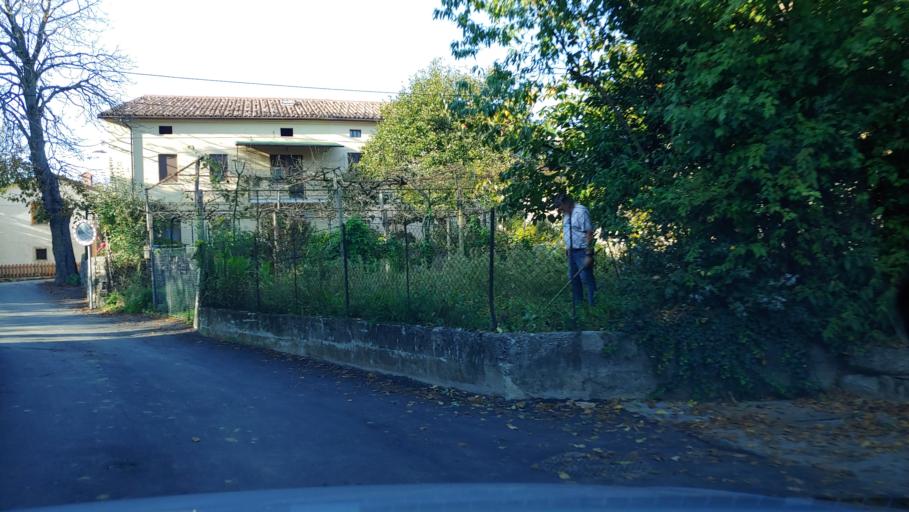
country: SI
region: Vipava
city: Vipava
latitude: 45.8360
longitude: 13.9341
